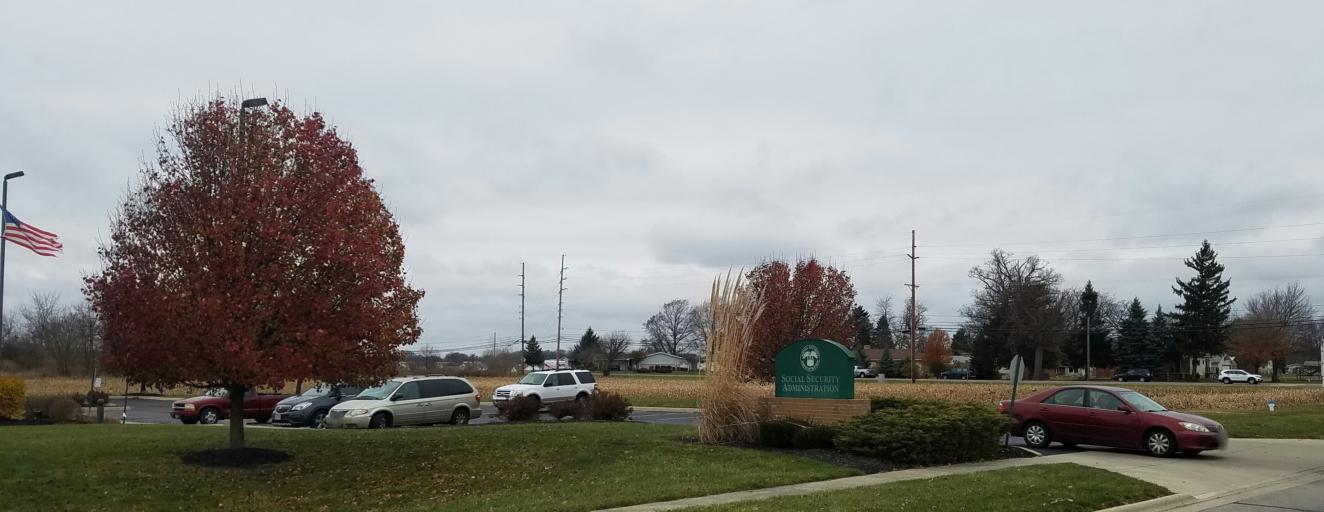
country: US
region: Ohio
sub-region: Marion County
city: Marion
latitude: 40.5629
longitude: -83.1078
